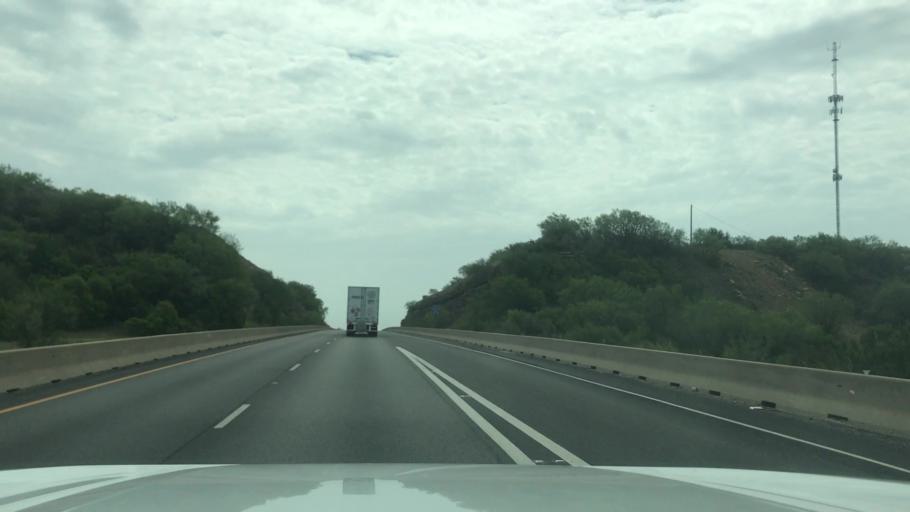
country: US
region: Texas
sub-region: Callahan County
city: Baird
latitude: 32.3955
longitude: -99.3649
